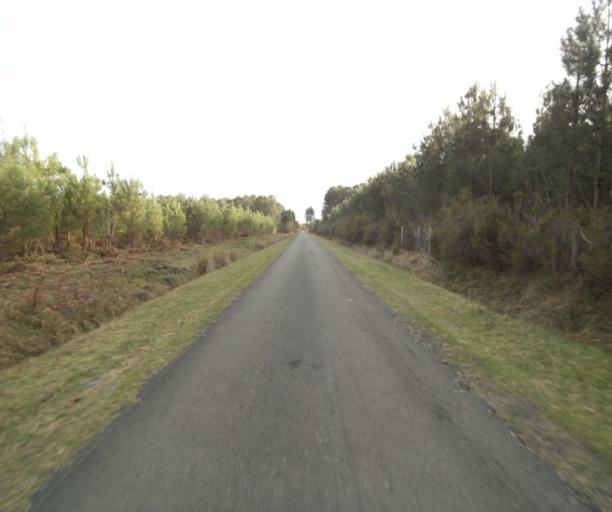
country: FR
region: Aquitaine
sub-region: Departement des Landes
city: Gabarret
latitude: 44.0568
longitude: 0.0516
